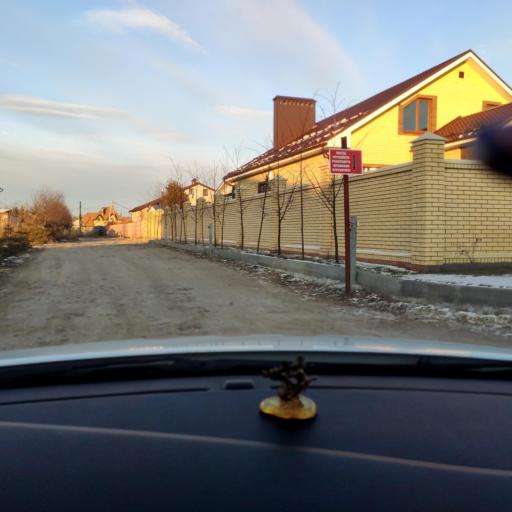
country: RU
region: Tatarstan
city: Stolbishchi
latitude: 55.6054
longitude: 49.1410
